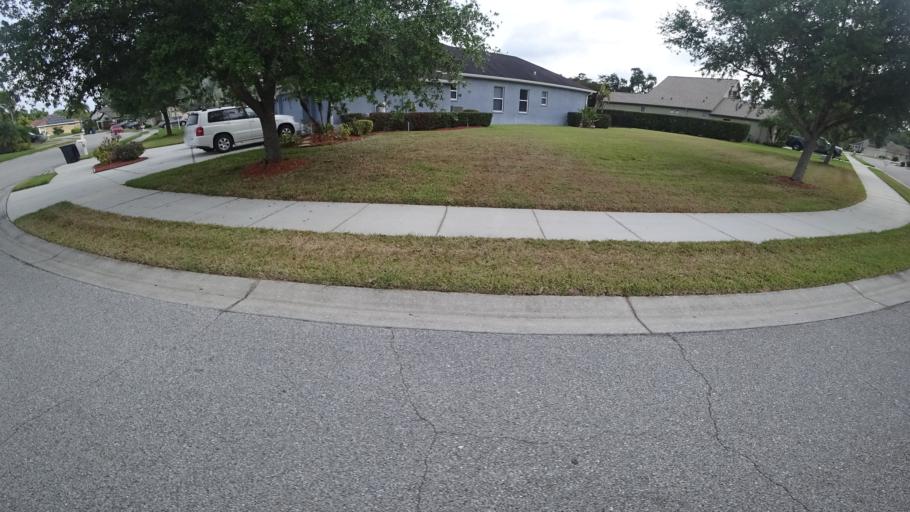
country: US
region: Florida
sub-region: Manatee County
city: Ellenton
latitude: 27.5621
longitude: -82.4694
